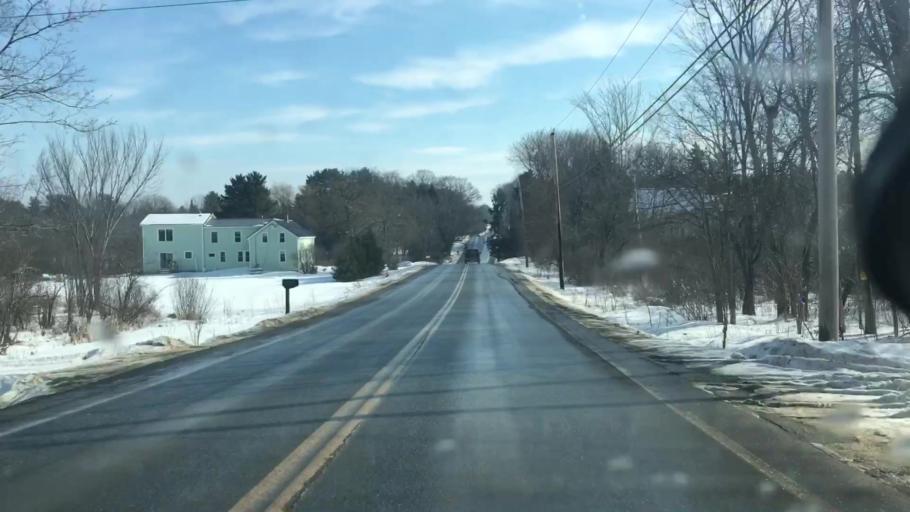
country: US
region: Maine
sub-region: Penobscot County
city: Bangor
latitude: 44.8453
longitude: -68.8361
